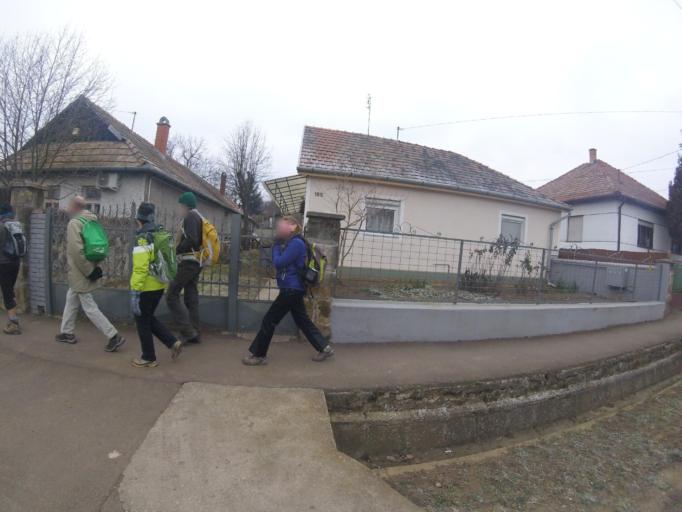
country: HU
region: Nograd
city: Paszto
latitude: 47.9499
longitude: 19.6947
